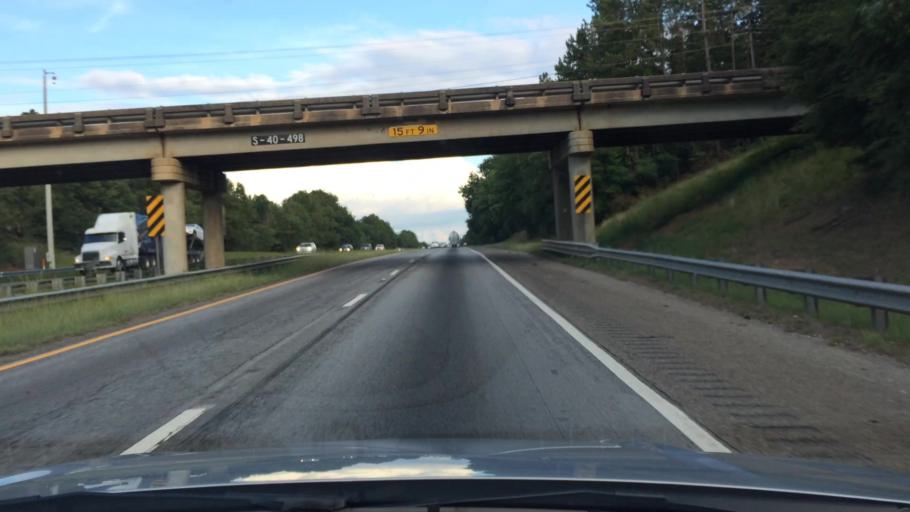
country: US
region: South Carolina
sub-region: Lexington County
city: Irmo
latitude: 34.1226
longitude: -81.1994
